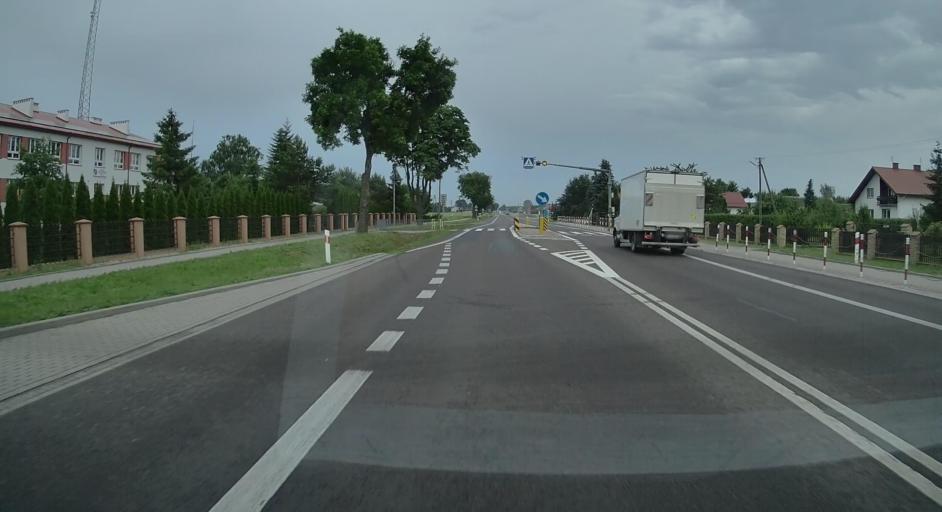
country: PL
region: Lublin Voivodeship
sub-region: Powiat bialski
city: Rzeczyca
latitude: 52.0269
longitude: 22.7123
